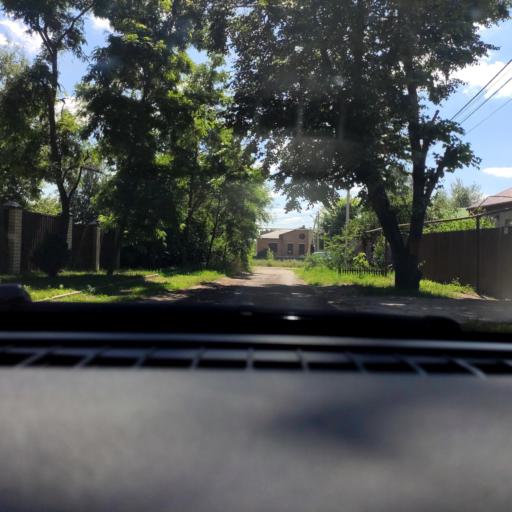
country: RU
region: Voronezj
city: Somovo
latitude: 51.6990
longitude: 39.3229
